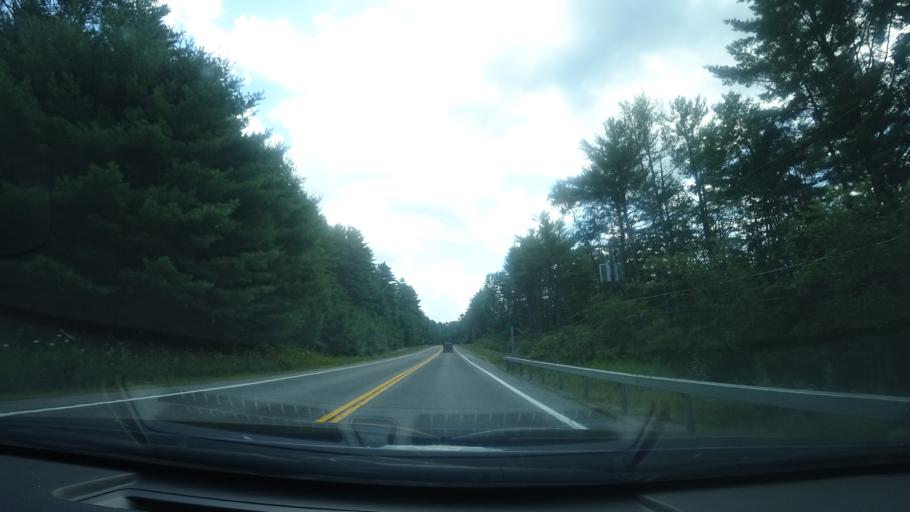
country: US
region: New York
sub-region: Warren County
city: Warrensburg
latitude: 43.6597
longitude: -73.8168
